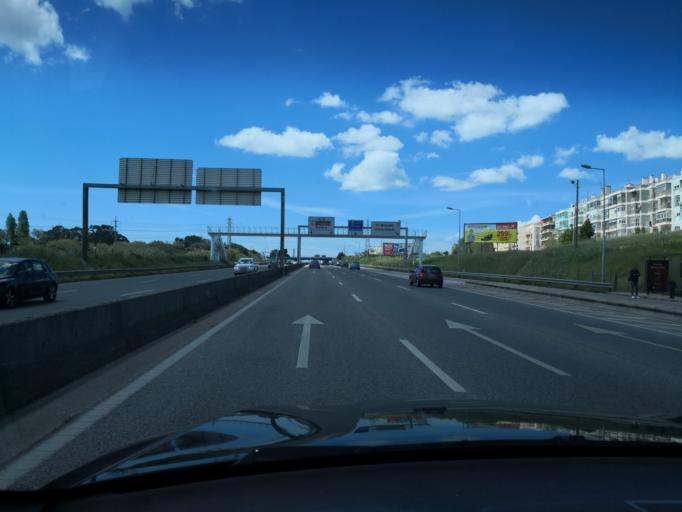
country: PT
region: Setubal
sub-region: Almada
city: Caparica
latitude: 38.6585
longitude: -9.1966
